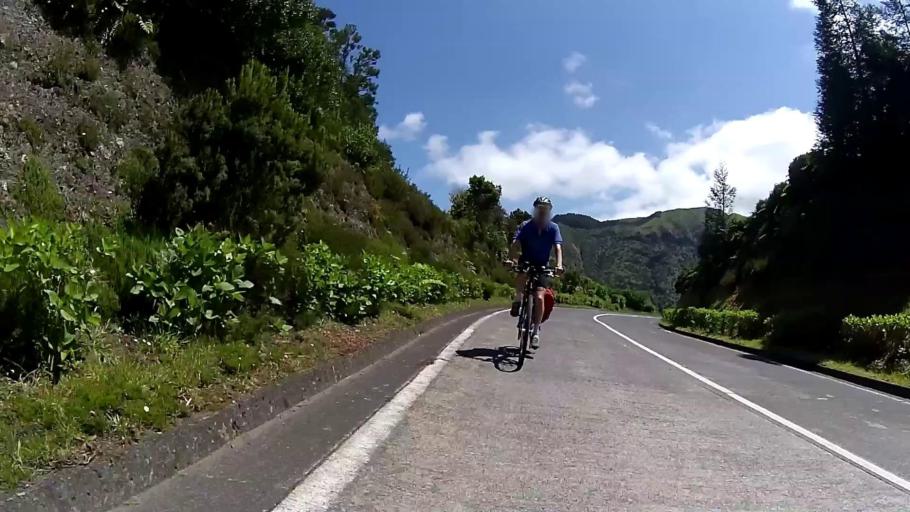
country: PT
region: Azores
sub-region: Ponta Delgada
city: Arrifes
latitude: 37.8540
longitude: -25.7739
